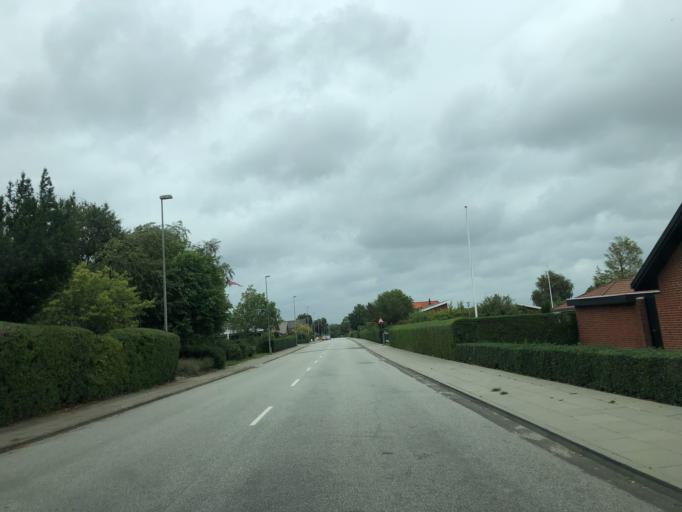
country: DK
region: Central Jutland
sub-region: Herning Kommune
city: Snejbjerg
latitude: 56.1270
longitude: 8.8969
